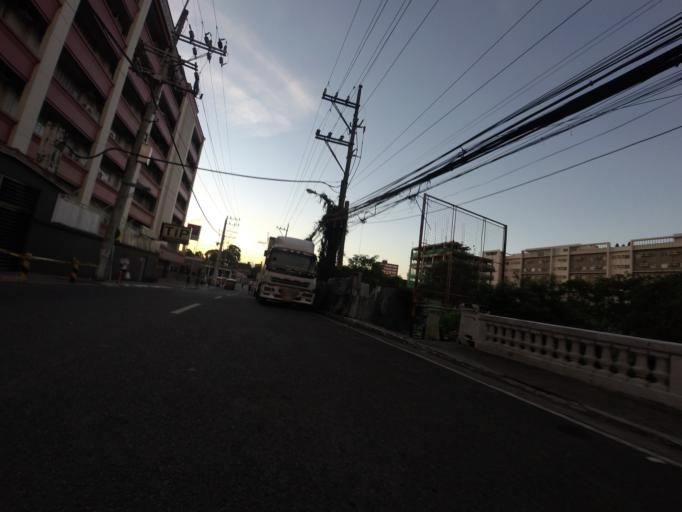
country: PH
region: Metro Manila
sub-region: City of Manila
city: Quiapo
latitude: 14.5965
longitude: 120.9907
